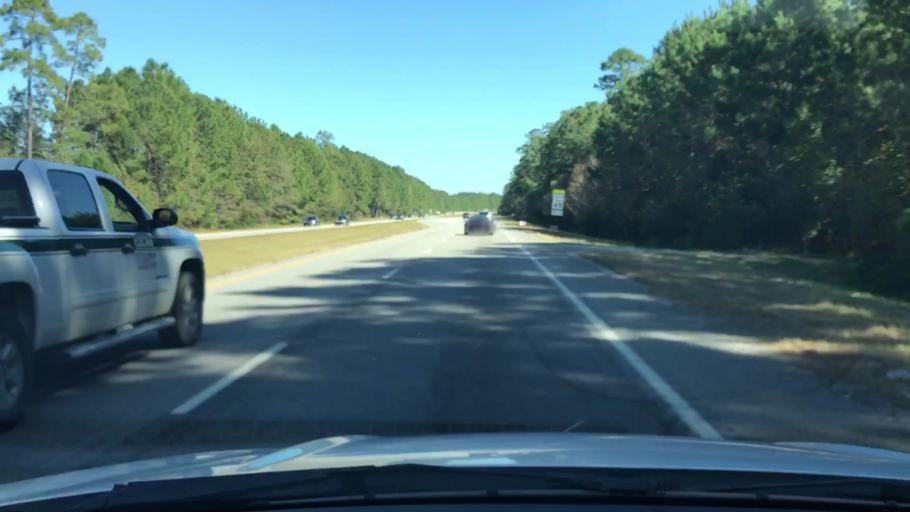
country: US
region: South Carolina
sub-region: Beaufort County
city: Bluffton
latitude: 32.3524
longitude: -80.9181
